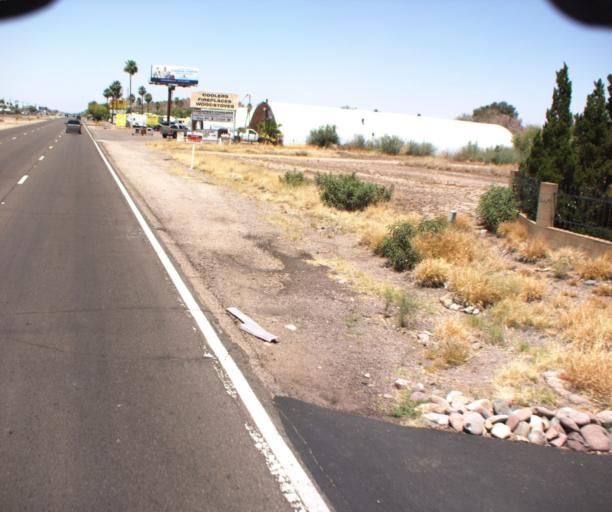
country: US
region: Arizona
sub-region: Pinal County
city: Apache Junction
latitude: 33.4154
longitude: -111.6384
